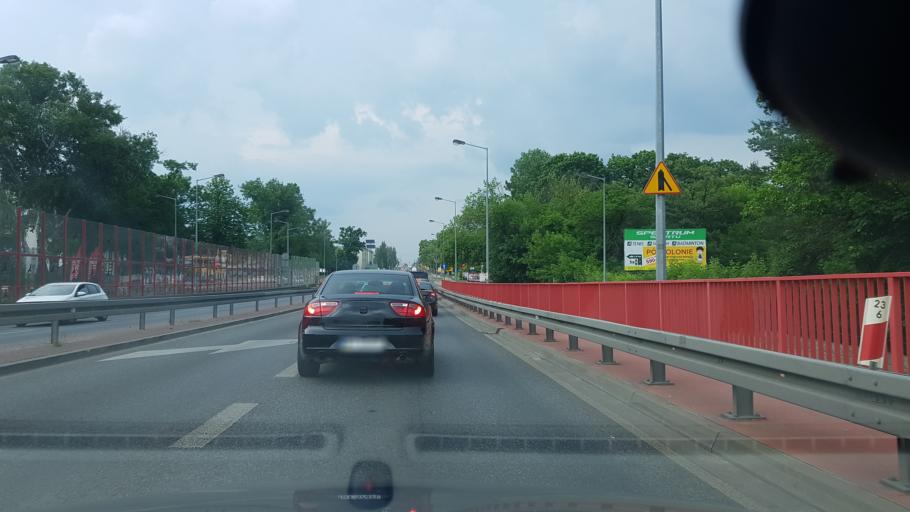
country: PL
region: Masovian Voivodeship
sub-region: Powiat legionowski
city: Legionowo
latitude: 52.4012
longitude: 20.9458
